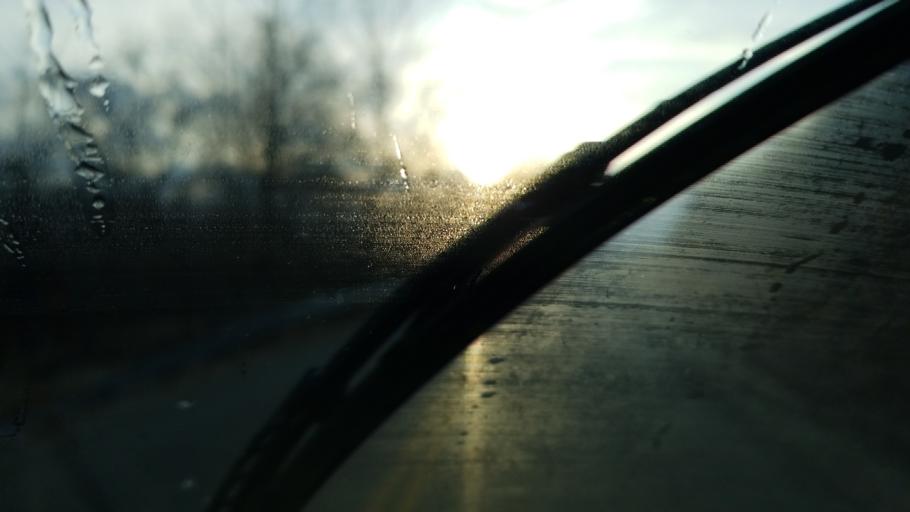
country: US
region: Ohio
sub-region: Ross County
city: Chillicothe
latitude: 39.2825
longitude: -82.9361
